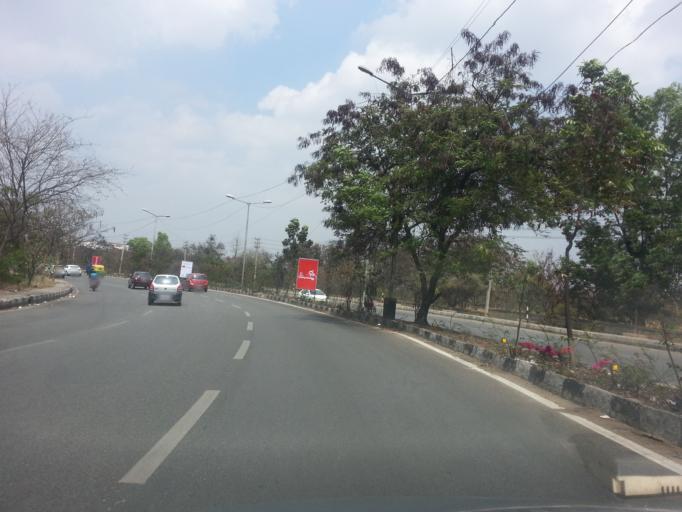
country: IN
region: Karnataka
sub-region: Bangalore Urban
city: Bangalore
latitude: 12.9469
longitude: 77.6407
